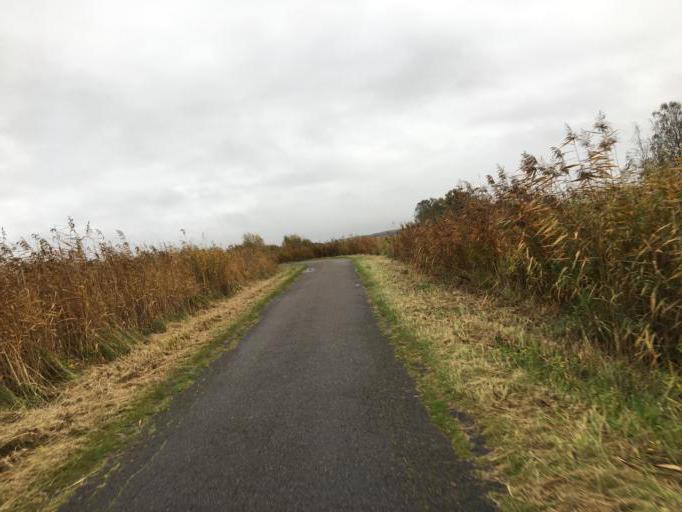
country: DK
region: Capital Region
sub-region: Tarnby Kommune
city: Tarnby
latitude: 55.6141
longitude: 12.5376
